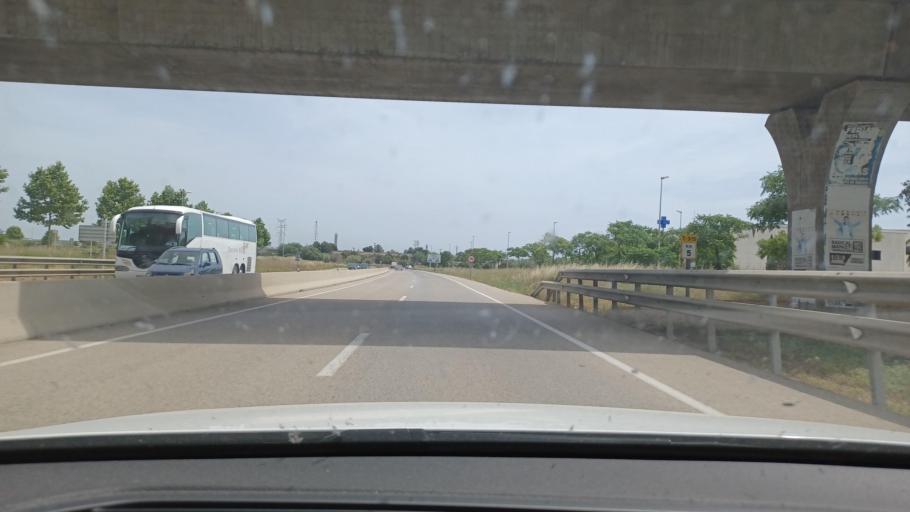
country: ES
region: Catalonia
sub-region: Provincia de Tarragona
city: Vila-seca
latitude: 41.1227
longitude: 1.1565
